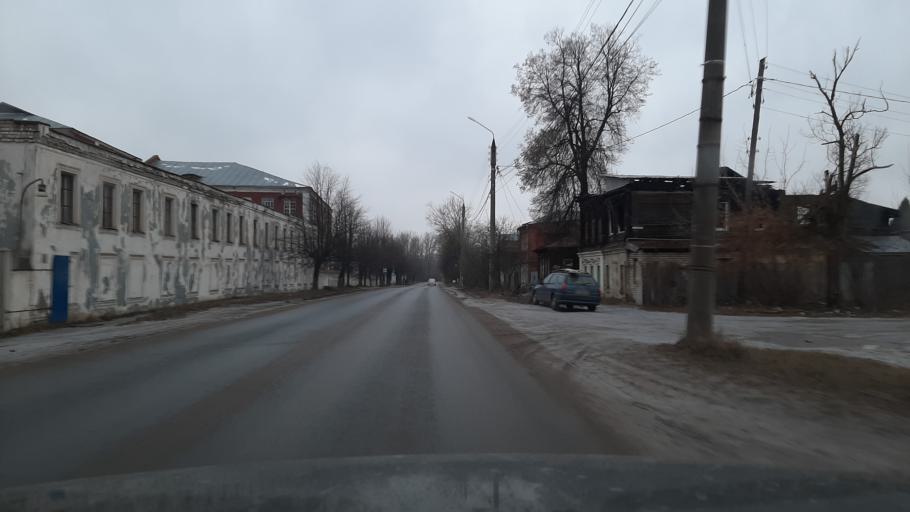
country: RU
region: Ivanovo
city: Shuya
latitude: 56.8591
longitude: 41.3651
